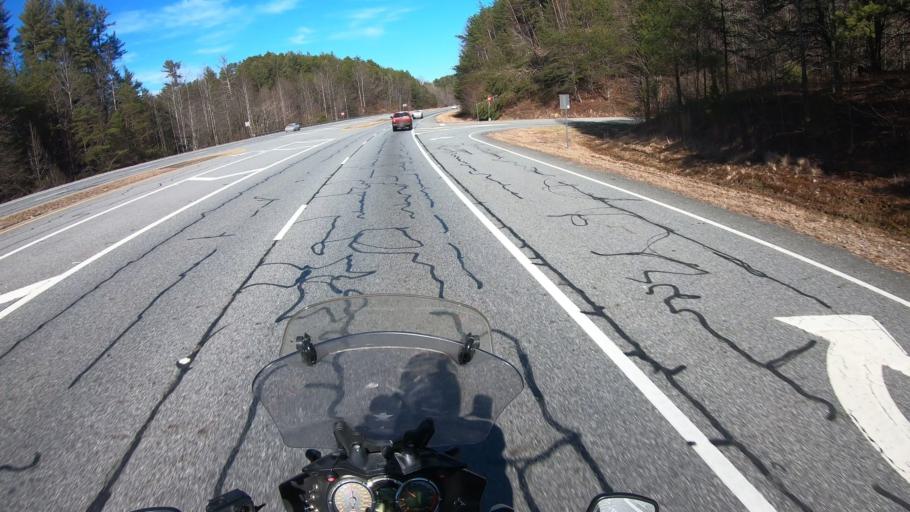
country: US
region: Georgia
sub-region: Fannin County
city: Blue Ridge
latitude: 34.7877
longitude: -84.3865
